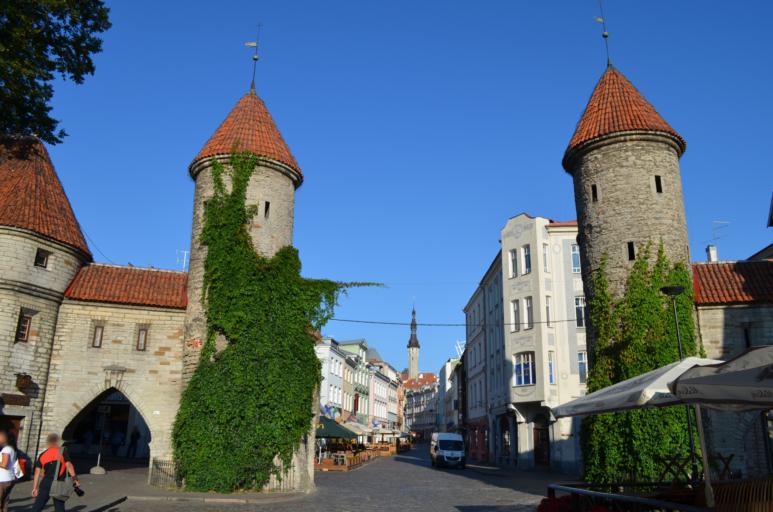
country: EE
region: Harju
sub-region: Tallinna linn
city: Tallinn
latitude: 59.4366
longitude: 24.7507
